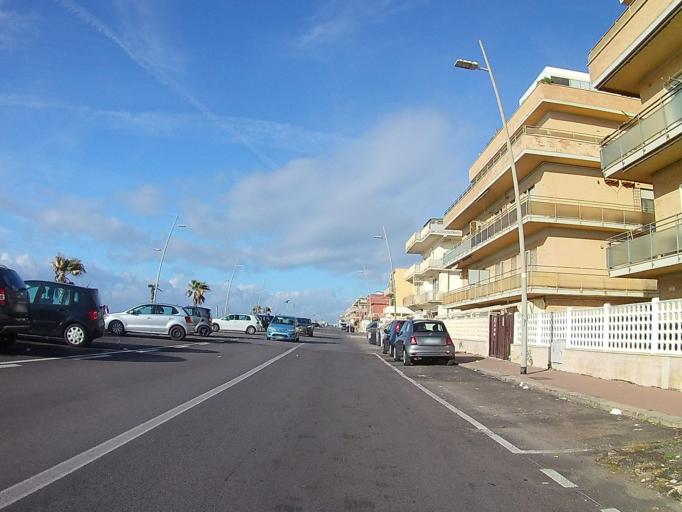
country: IT
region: Latium
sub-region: Citta metropolitana di Roma Capitale
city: Lido di Ostia
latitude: 41.7339
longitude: 12.2636
